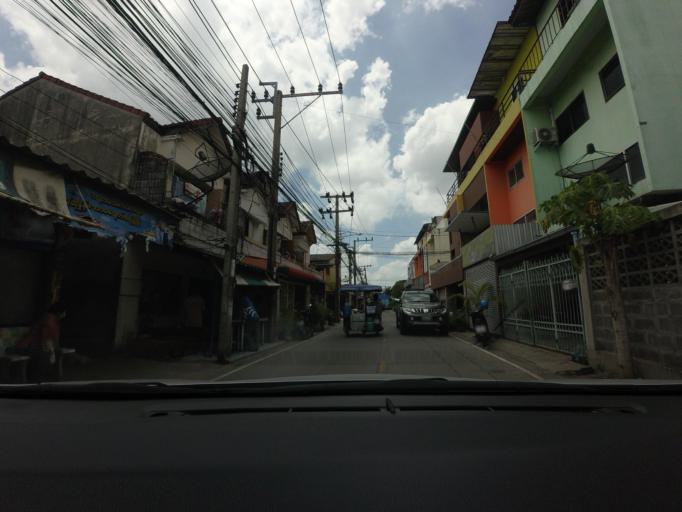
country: TH
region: Samut Prakan
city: Phra Samut Chedi
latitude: 13.6254
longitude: 100.5571
